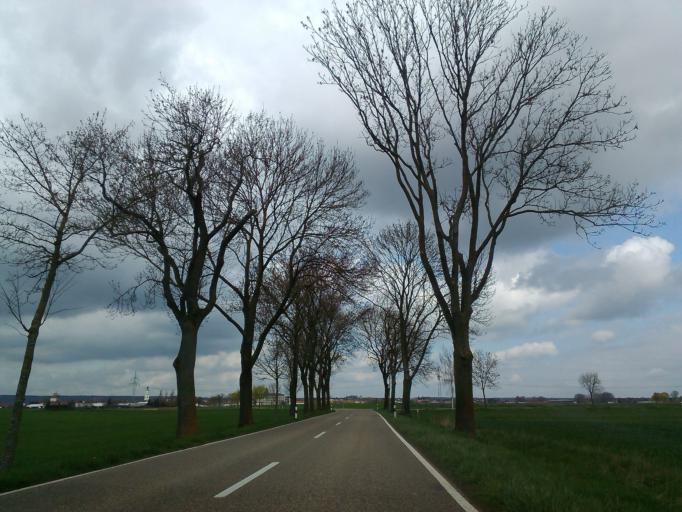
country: DE
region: Baden-Wuerttemberg
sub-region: Tuebingen Region
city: Langenau
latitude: 48.4867
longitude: 10.1393
